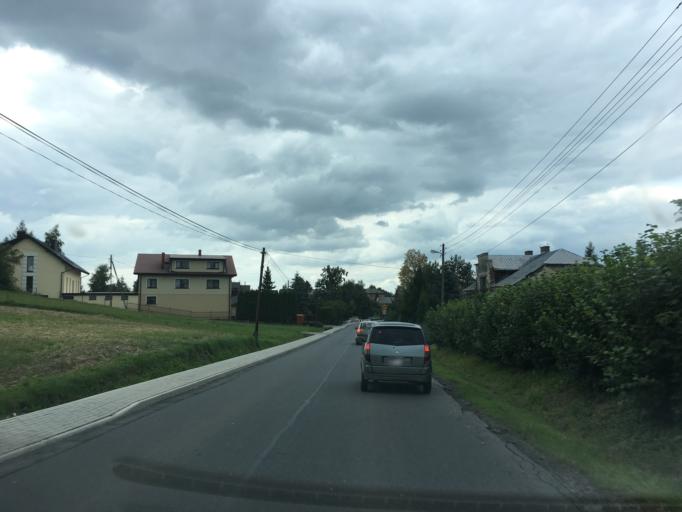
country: PL
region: Lesser Poland Voivodeship
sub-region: Powiat olkuski
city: Wolbrom
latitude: 50.4041
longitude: 19.7676
